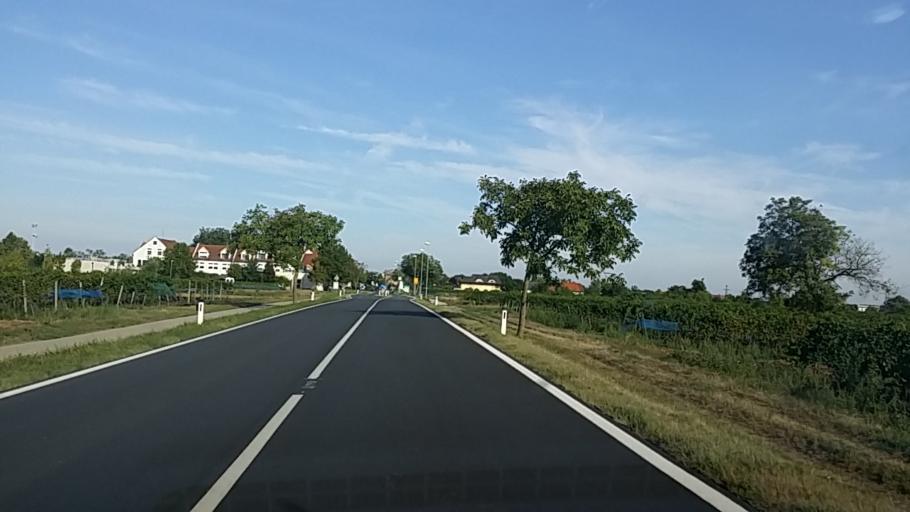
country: AT
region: Burgenland
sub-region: Politischer Bezirk Neusiedl am See
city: Illmitz
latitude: 47.7572
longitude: 16.8121
